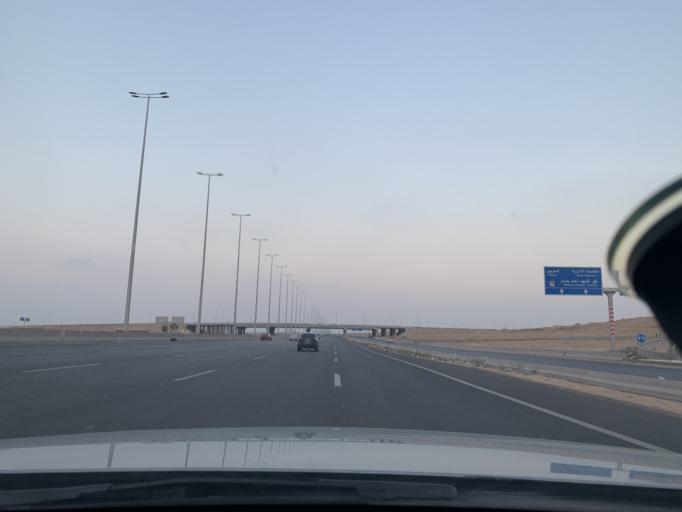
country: EG
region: Muhafazat al Qalyubiyah
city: Al Khankah
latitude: 30.0915
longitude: 31.5016
